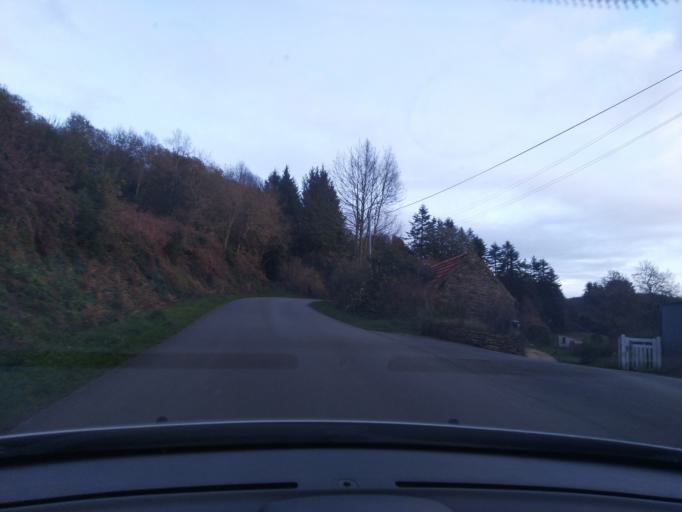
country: FR
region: Brittany
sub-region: Departement du Finistere
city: Guerlesquin
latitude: 48.5380
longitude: -3.6161
